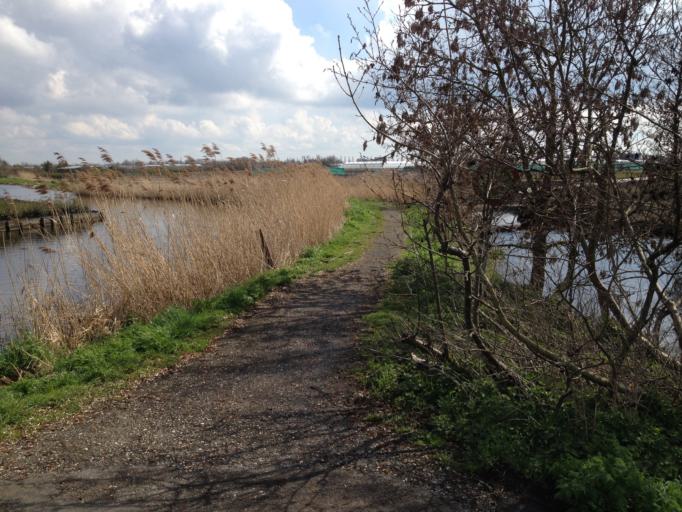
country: NL
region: South Holland
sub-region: Gemeente Boskoop
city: Boskoop
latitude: 52.0872
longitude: 4.6322
